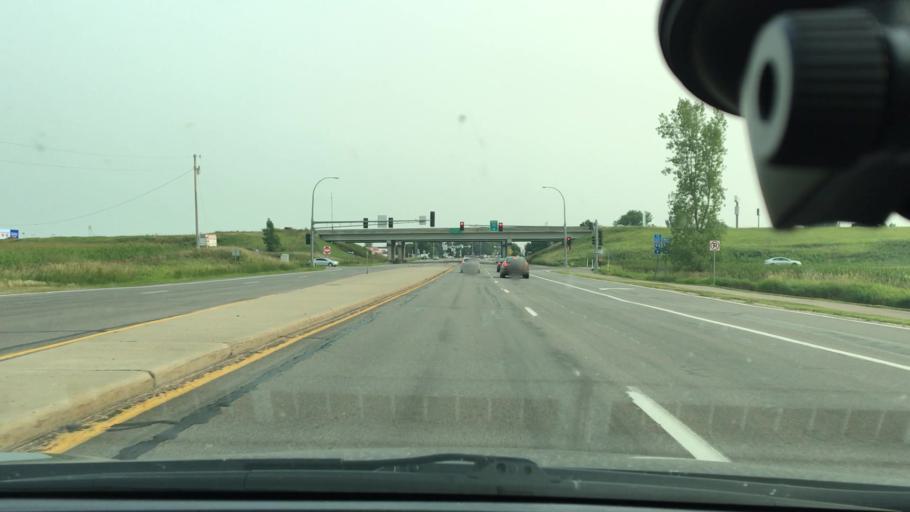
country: US
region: Minnesota
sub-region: Wright County
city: Albertville
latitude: 45.2432
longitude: -93.6634
